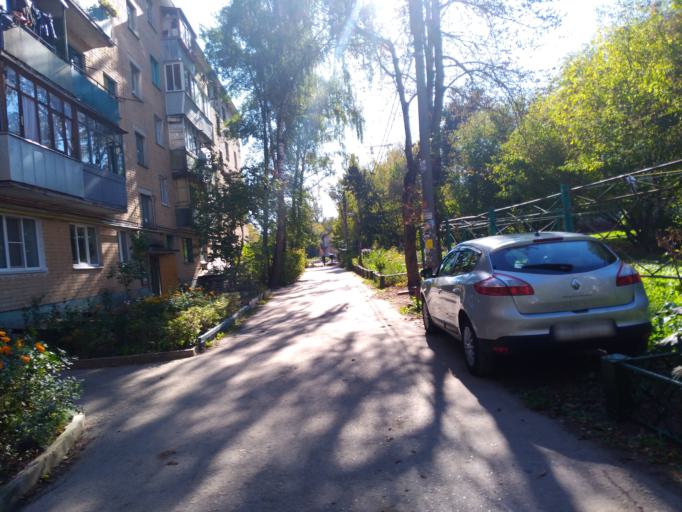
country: RU
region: Kaluga
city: Kaluga
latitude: 54.5289
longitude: 36.2661
